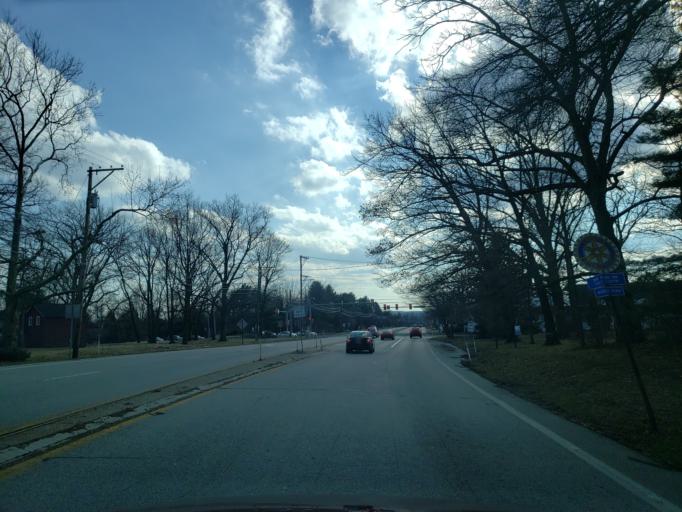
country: US
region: Pennsylvania
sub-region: Montgomery County
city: North Wales
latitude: 40.2031
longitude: -75.2552
